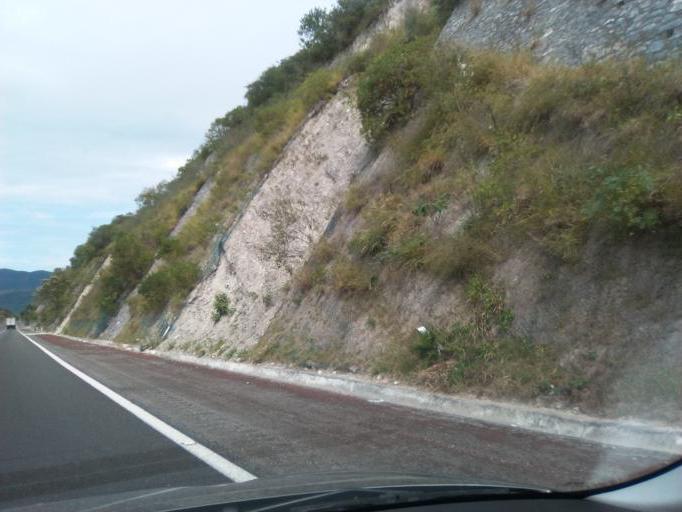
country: MX
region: Guerrero
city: Zumpango del Rio
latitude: 17.6166
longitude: -99.5199
